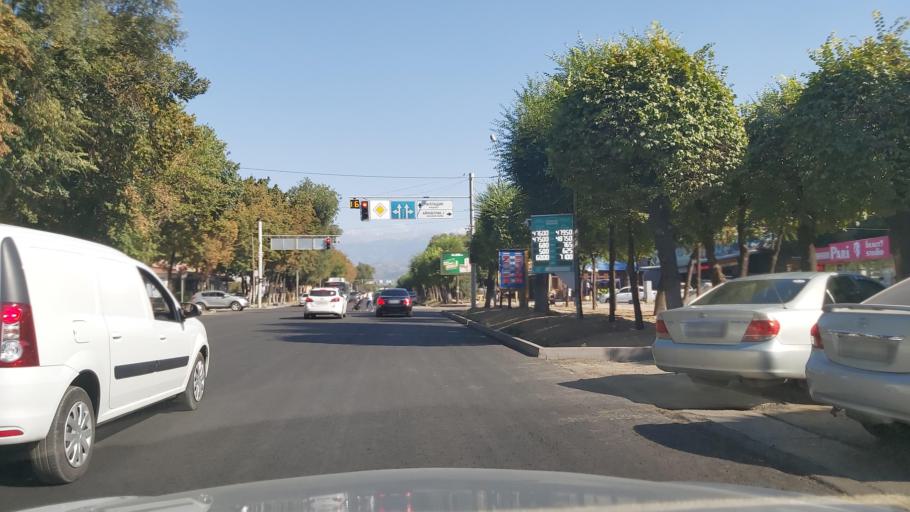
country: KZ
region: Almaty Oblysy
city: Pervomayskiy
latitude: 43.3232
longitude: 76.9115
